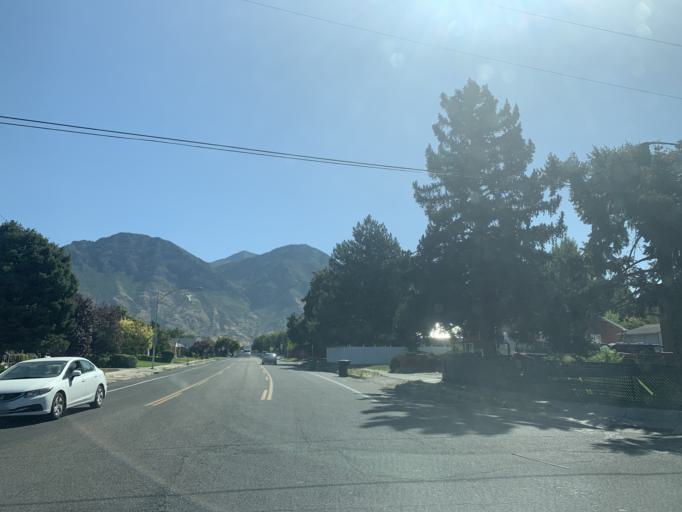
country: US
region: Utah
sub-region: Utah County
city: Provo
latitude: 40.2444
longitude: -111.6729
